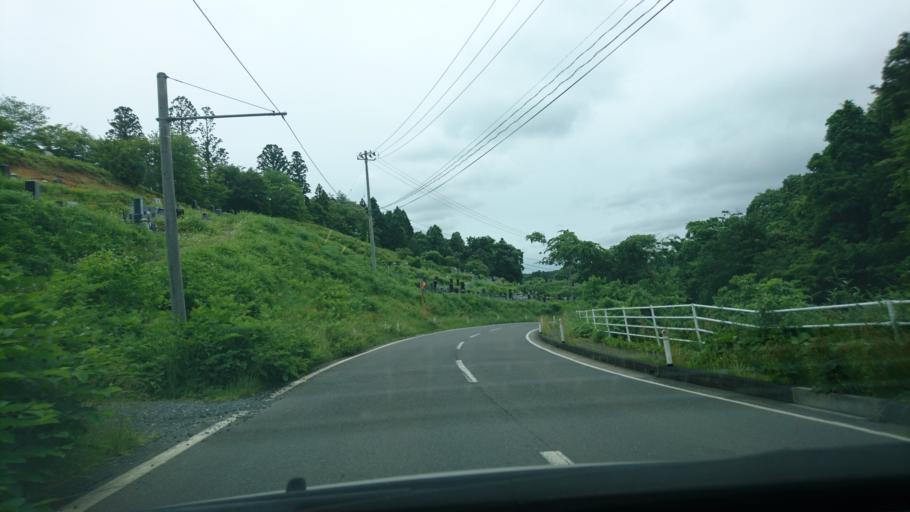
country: JP
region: Iwate
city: Ichinoseki
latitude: 38.9535
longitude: 141.0536
